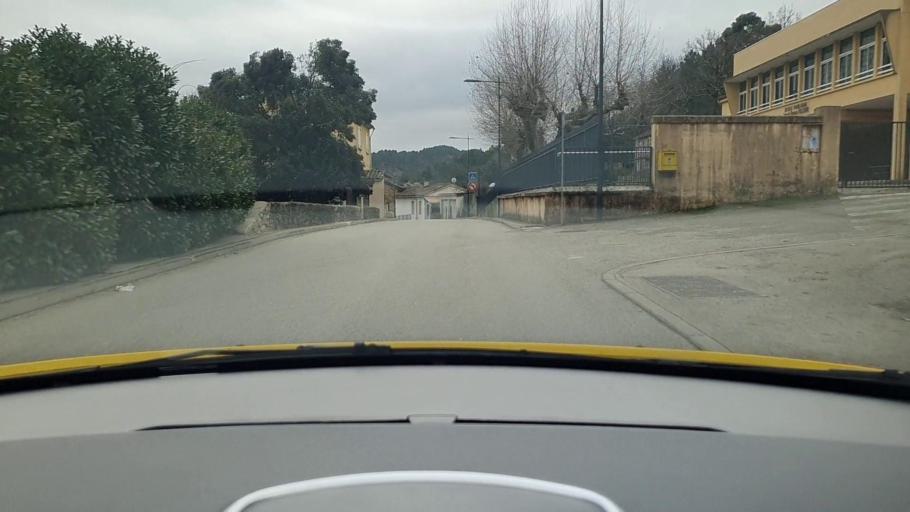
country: FR
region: Languedoc-Roussillon
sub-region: Departement du Gard
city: Les Salles-du-Gardon
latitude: 44.2474
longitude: 4.0492
